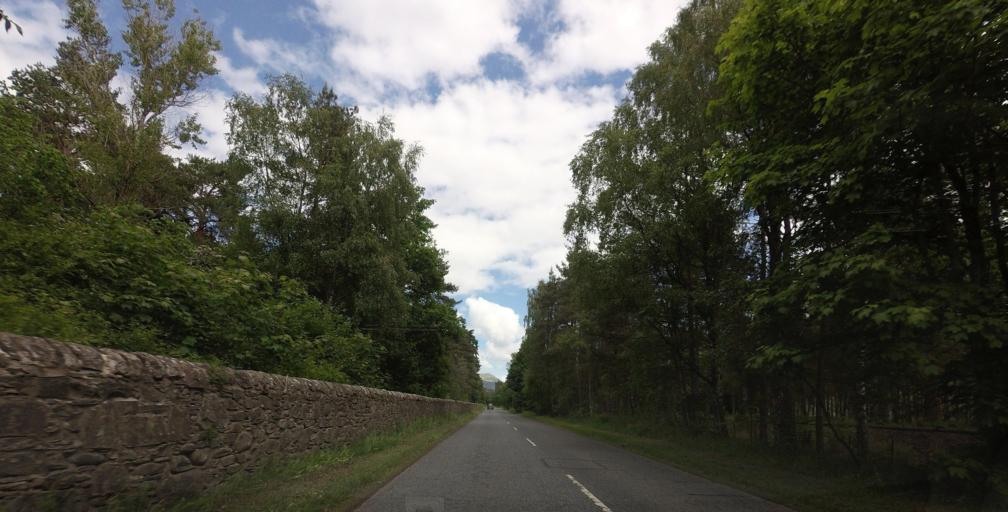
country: GB
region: Scotland
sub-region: Perth and Kinross
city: Aberfeldy
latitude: 56.7681
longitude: -3.8761
